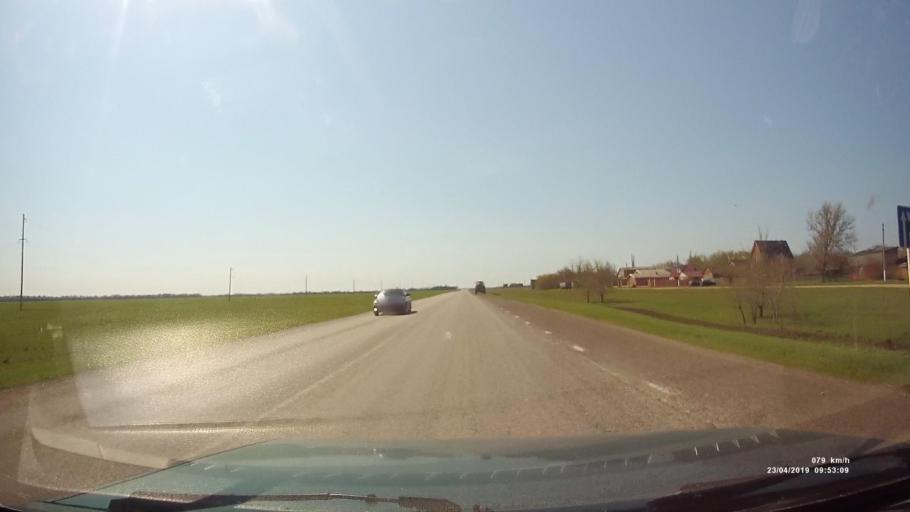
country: RU
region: Rostov
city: Orlovskiy
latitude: 46.8356
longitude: 42.0495
